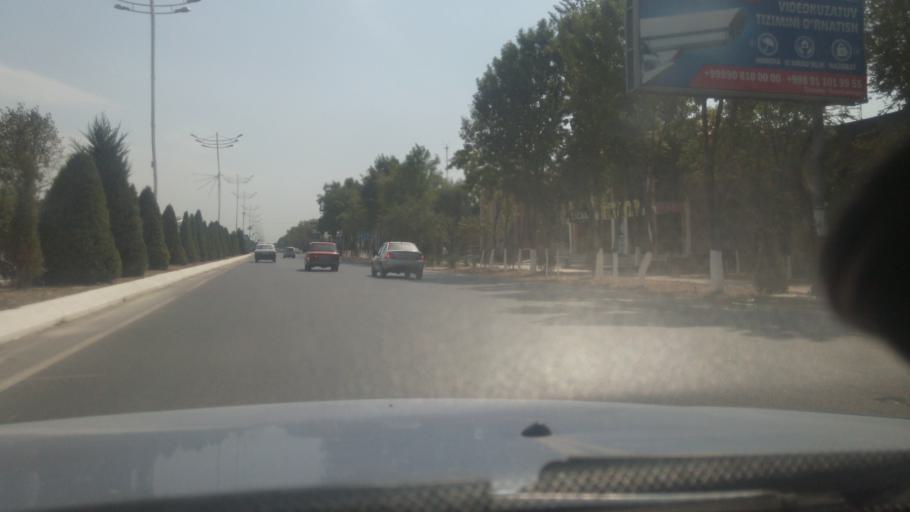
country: UZ
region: Sirdaryo
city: Guliston
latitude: 40.5005
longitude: 68.7738
